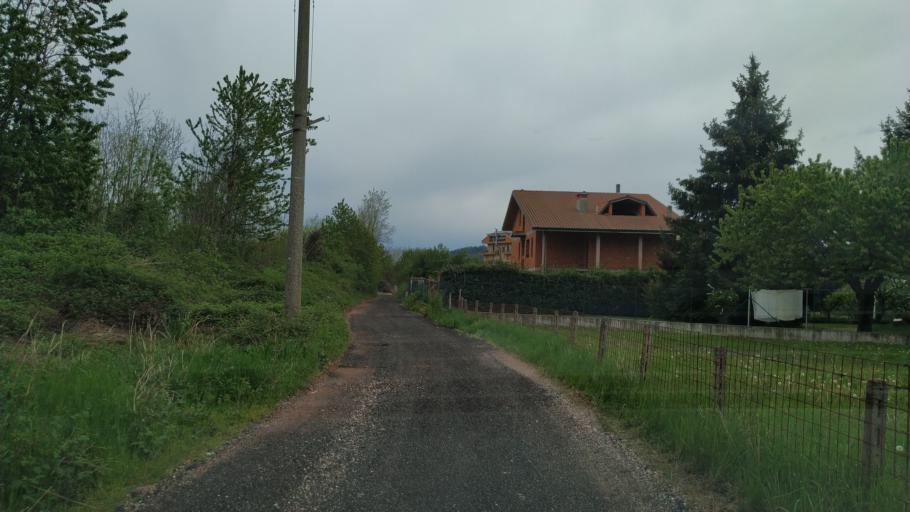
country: IT
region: Piedmont
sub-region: Provincia di Novara
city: Grignasco
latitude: 45.6752
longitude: 8.3470
